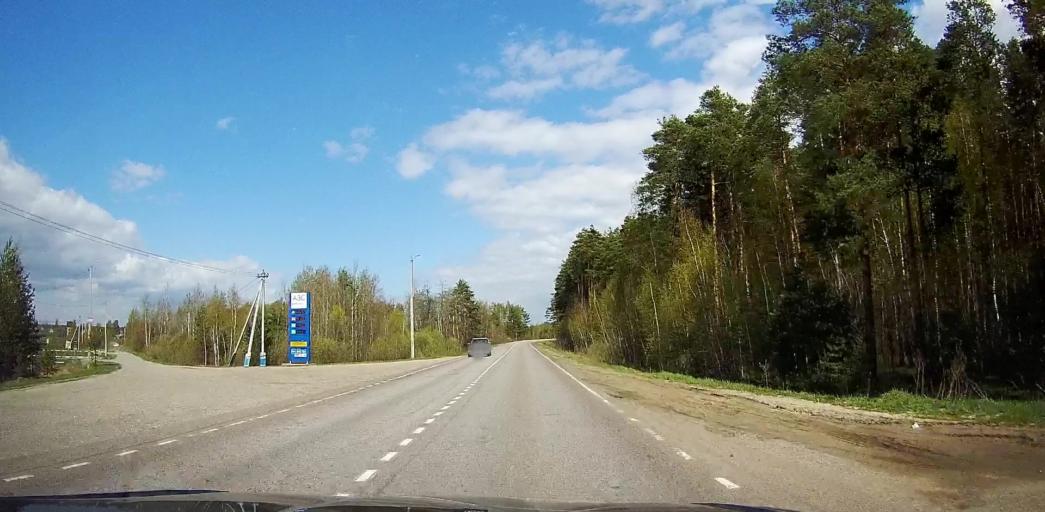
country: RU
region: Moskovskaya
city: Davydovo
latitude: 55.5500
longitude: 38.8177
